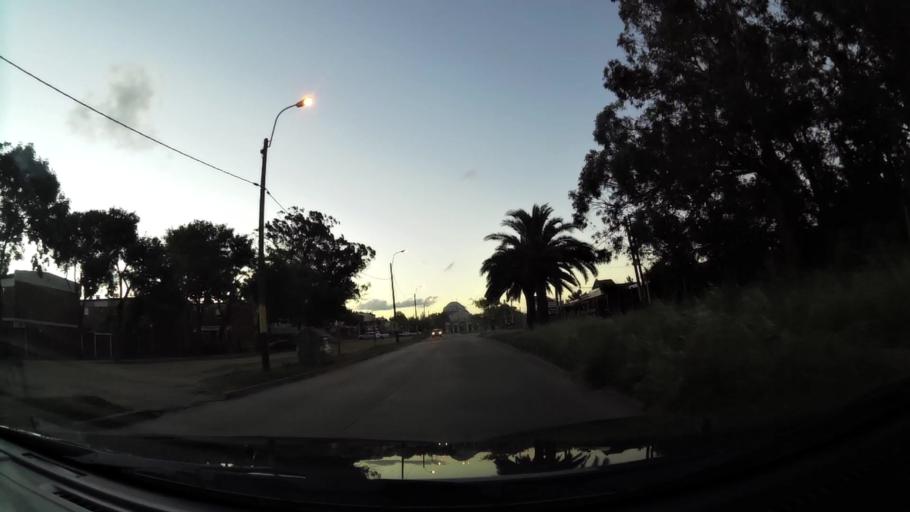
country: UY
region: Canelones
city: Paso de Carrasco
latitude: -34.8734
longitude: -56.0948
